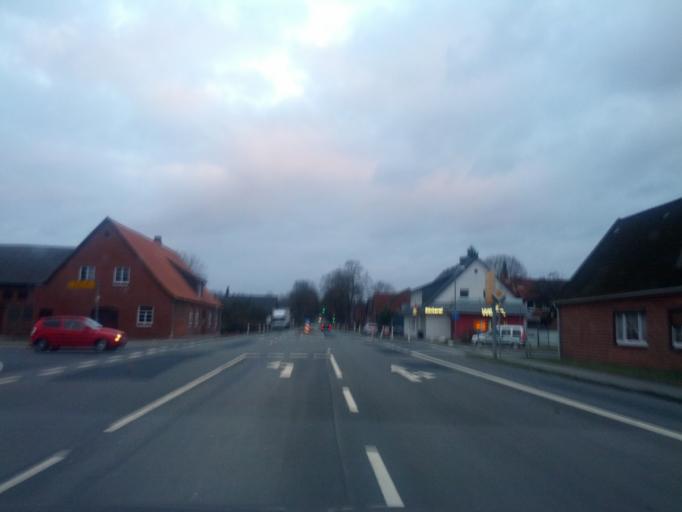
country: DE
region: Lower Saxony
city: Wistedt
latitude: 53.2706
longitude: 9.6812
